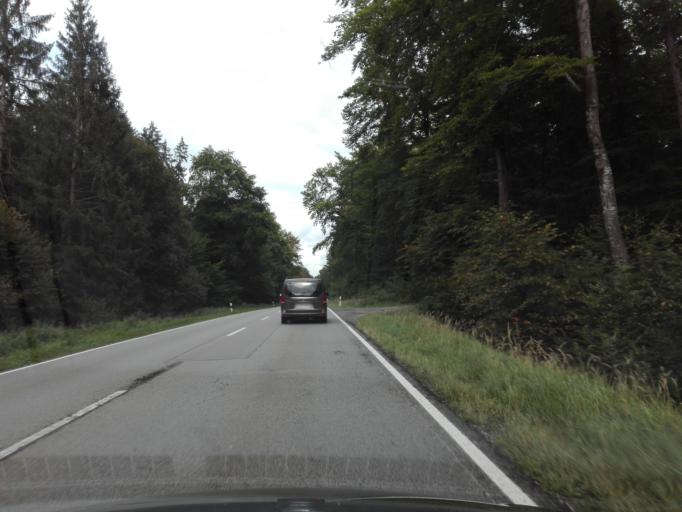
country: DE
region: Bavaria
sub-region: Upper Bavaria
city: Maitenbeth
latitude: 48.1450
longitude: 12.0696
